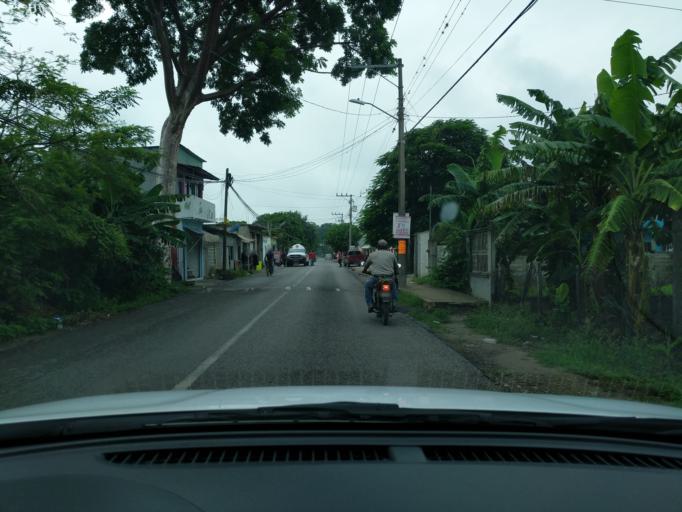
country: MX
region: Tabasco
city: Villahermosa
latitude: 17.9558
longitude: -92.9649
